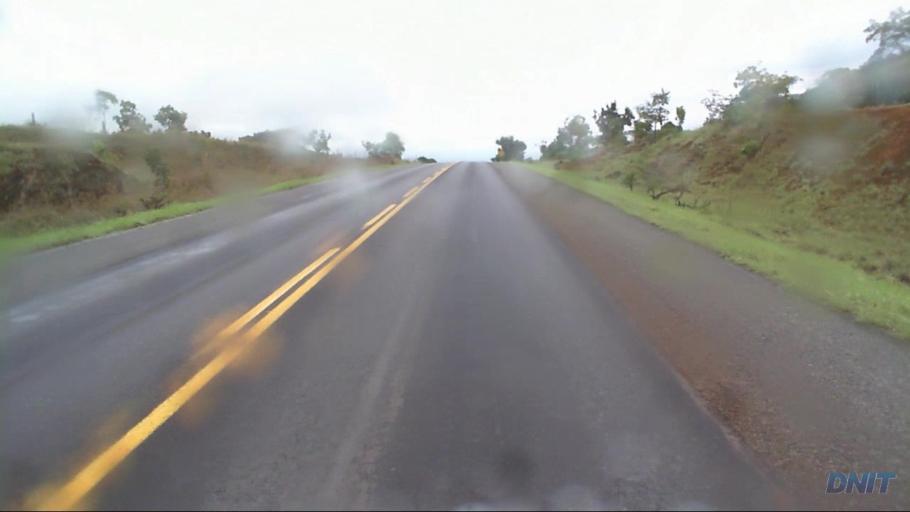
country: BR
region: Goias
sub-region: Padre Bernardo
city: Padre Bernardo
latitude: -15.1957
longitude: -48.4425
